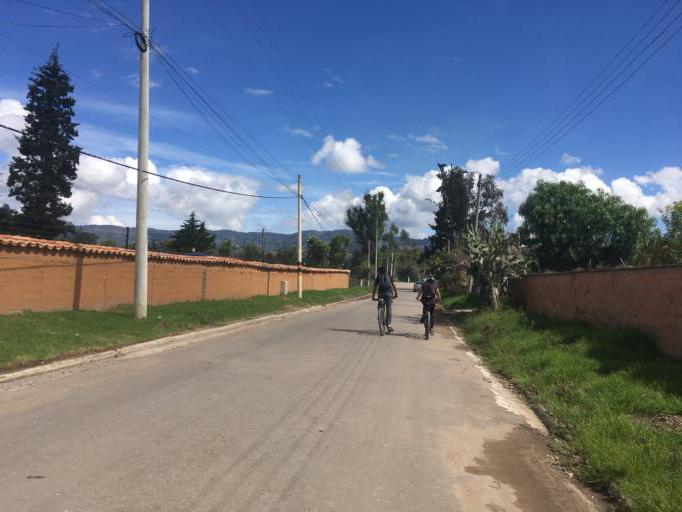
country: CO
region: Boyaca
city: Firavitoba
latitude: 5.6681
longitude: -72.9625
